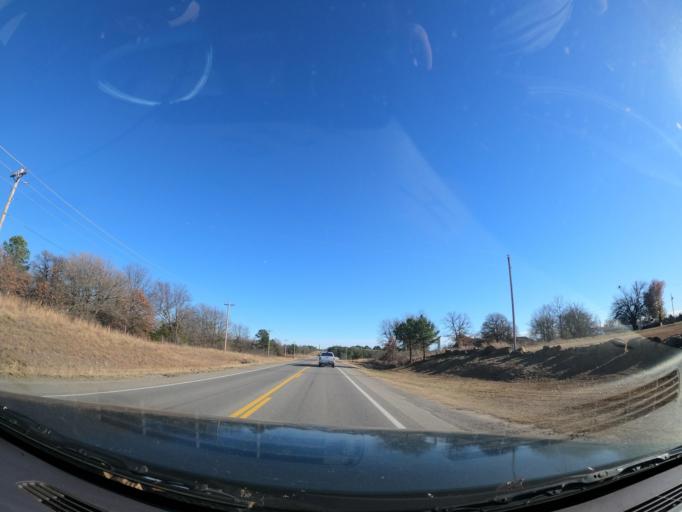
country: US
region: Oklahoma
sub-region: Pittsburg County
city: Longtown
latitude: 35.2344
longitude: -95.4620
